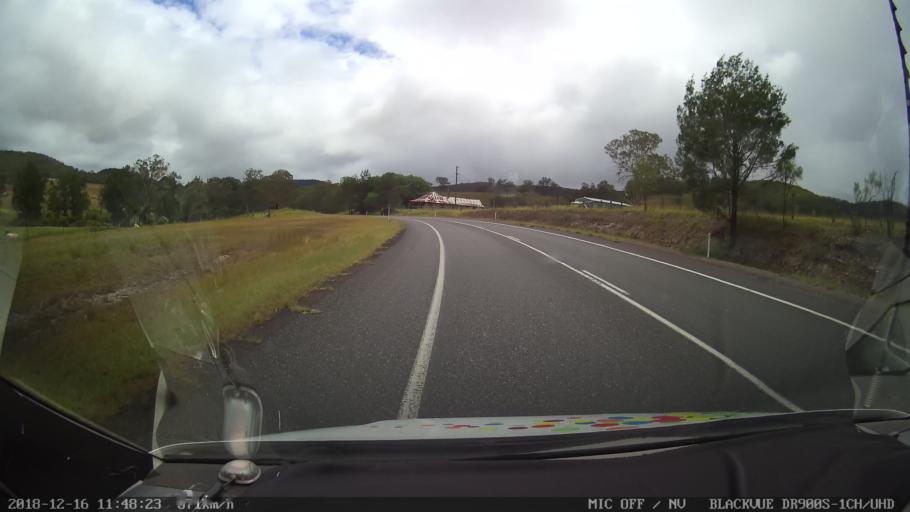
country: AU
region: New South Wales
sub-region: Tenterfield Municipality
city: Carrolls Creek
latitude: -28.9227
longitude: 152.2470
